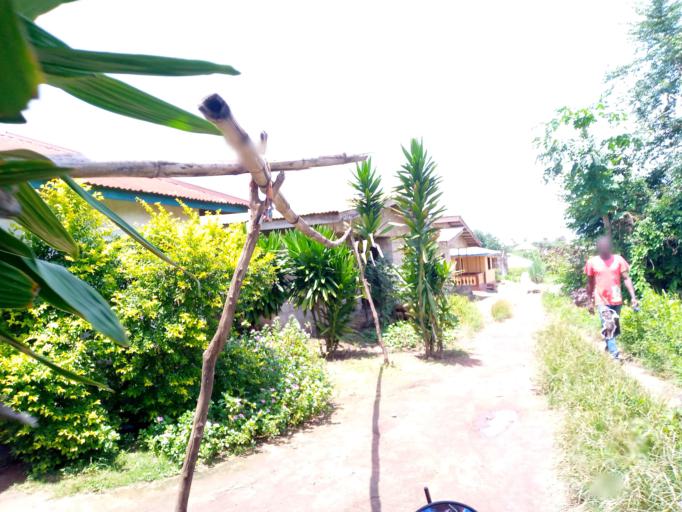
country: SL
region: Northern Province
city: Magburaka
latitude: 8.7237
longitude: -11.9263
